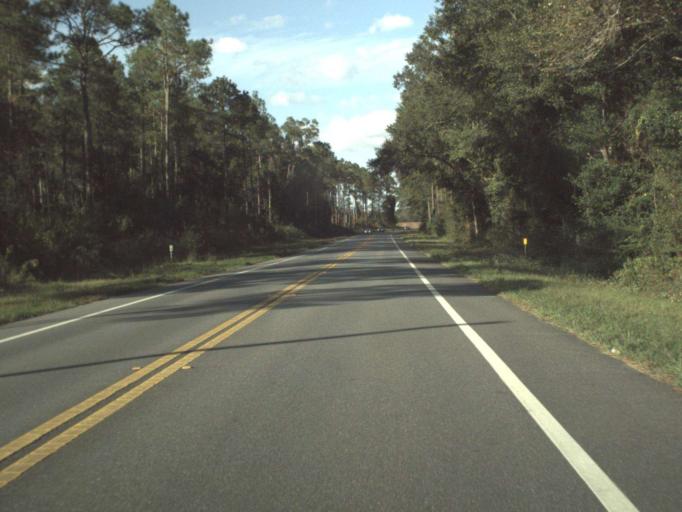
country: US
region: Florida
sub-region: Holmes County
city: Bonifay
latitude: 30.7177
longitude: -85.6163
